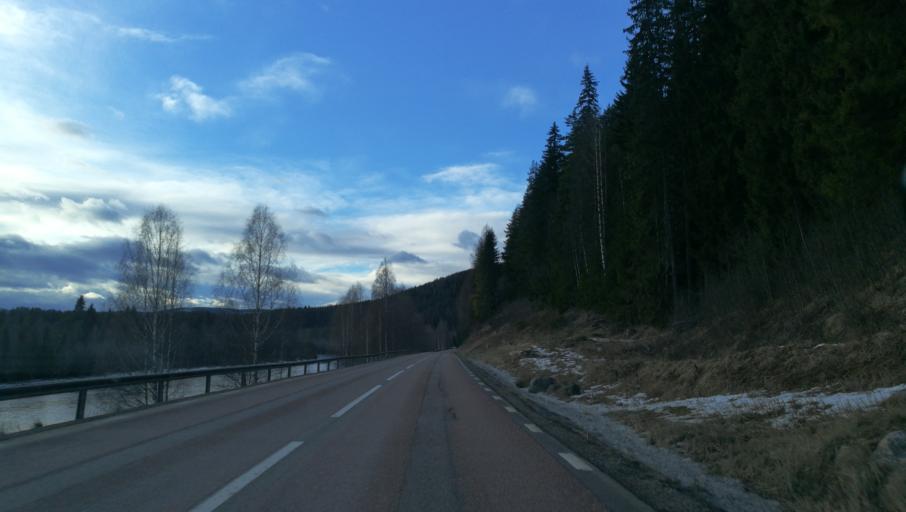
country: SE
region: Vaermland
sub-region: Torsby Kommun
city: Torsby
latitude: 60.7475
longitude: 12.8150
